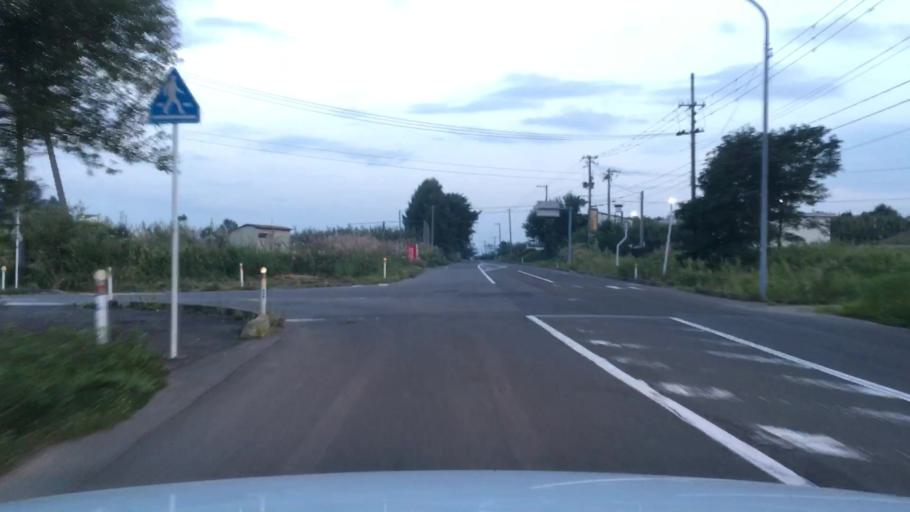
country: JP
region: Aomori
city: Hirosaki
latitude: 40.6782
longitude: 140.3734
